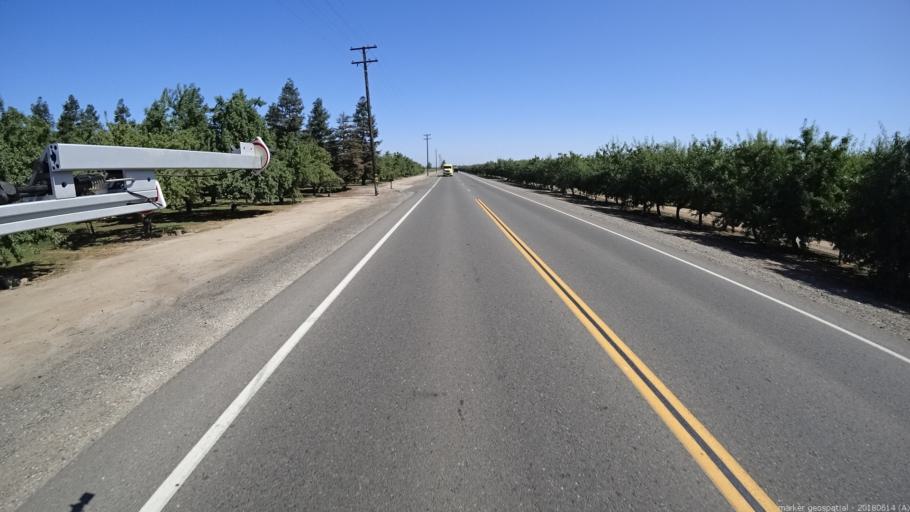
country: US
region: California
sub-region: Madera County
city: Madera
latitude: 36.9693
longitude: -120.1285
